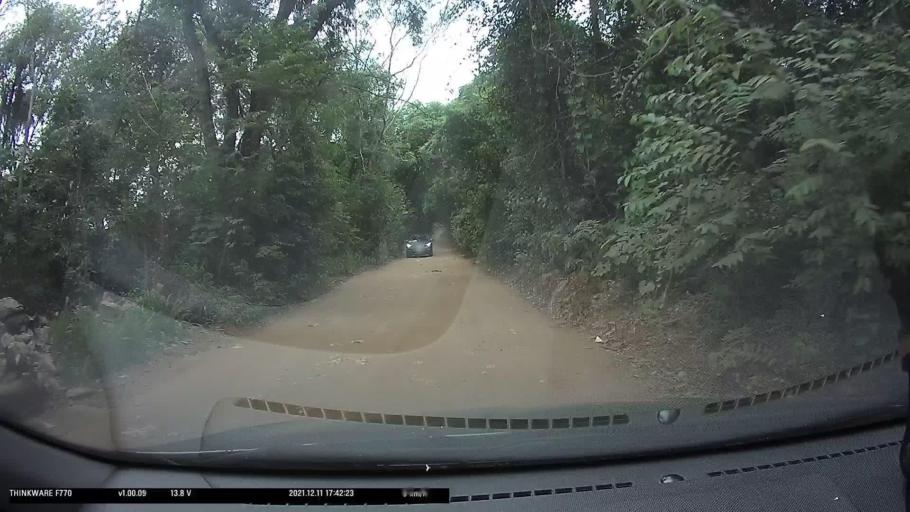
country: PY
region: Cordillera
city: San Bernardino
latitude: -25.2946
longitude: -57.2660
